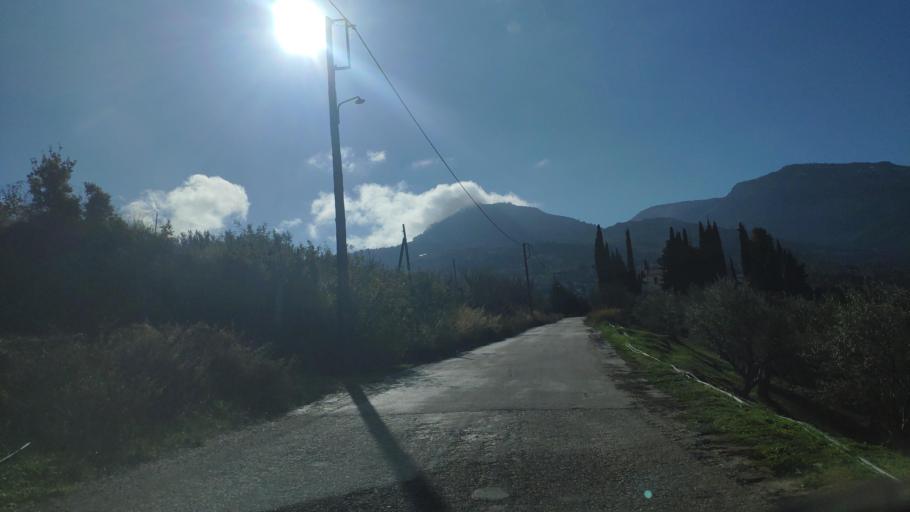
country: GR
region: West Greece
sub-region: Nomos Achaias
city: Aiyira
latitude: 38.0958
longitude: 22.4401
